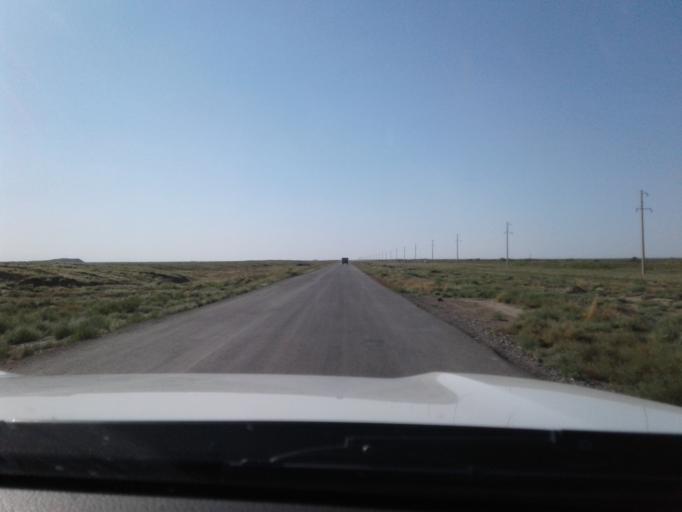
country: IR
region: Razavi Khorasan
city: Kalat-e Naderi
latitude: 37.1389
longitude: 60.0725
